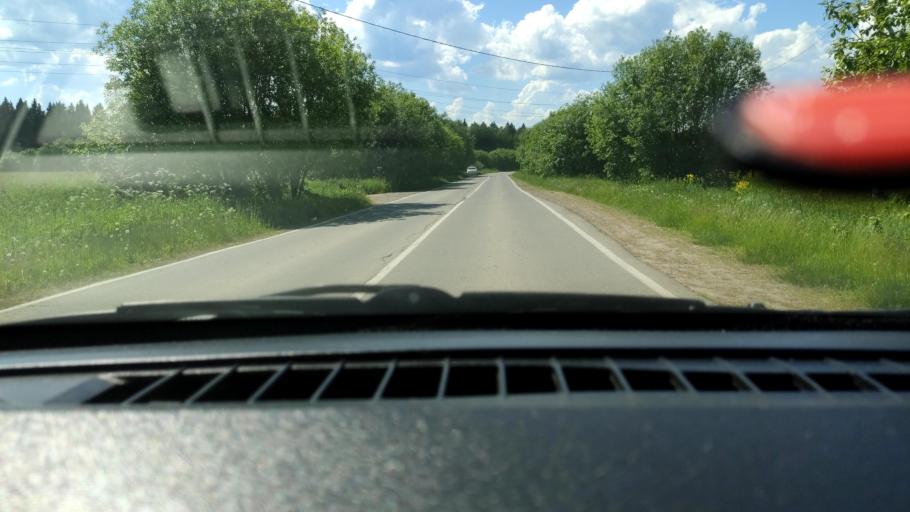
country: RU
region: Perm
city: Sylva
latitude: 58.0143
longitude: 56.7585
